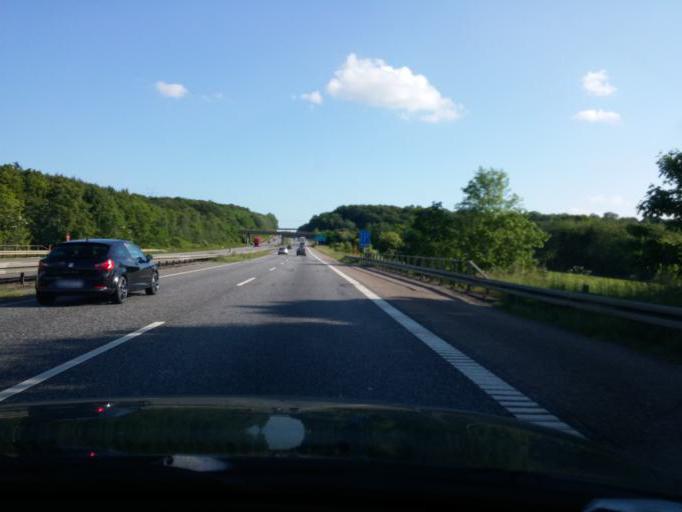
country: DK
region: South Denmark
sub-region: Kolding Kommune
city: Kolding
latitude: 55.4969
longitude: 9.4203
